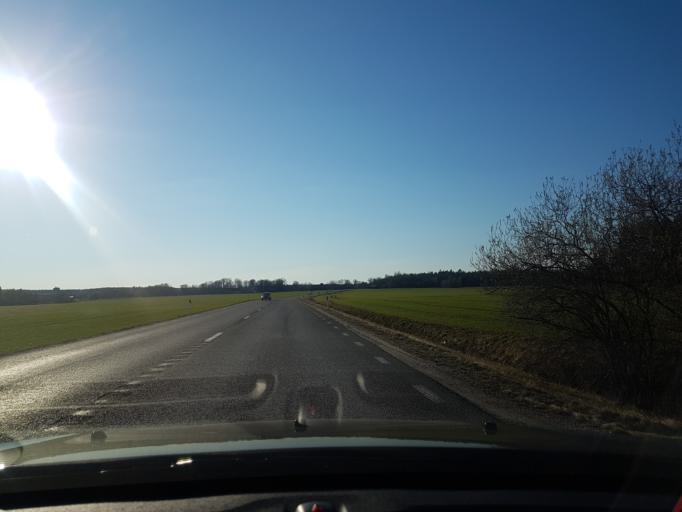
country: SE
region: Uppsala
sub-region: Enkopings Kommun
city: Orsundsbro
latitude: 59.8714
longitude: 17.3055
